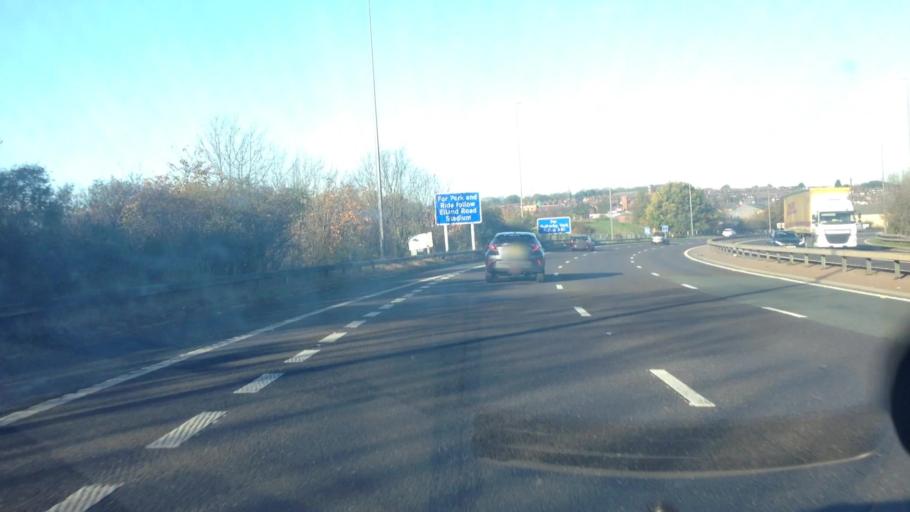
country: GB
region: England
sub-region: City and Borough of Leeds
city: Leeds
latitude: 53.7705
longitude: -1.5364
